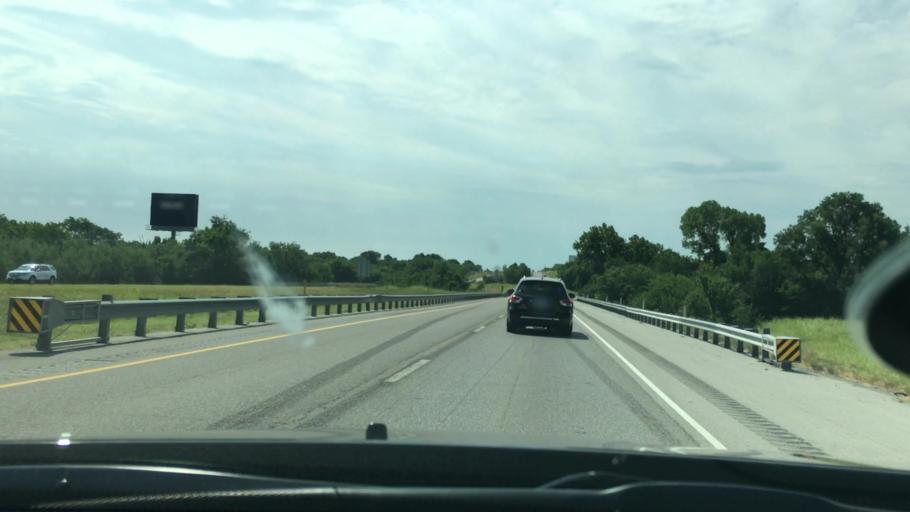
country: US
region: Oklahoma
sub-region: Murray County
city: Davis
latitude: 34.5021
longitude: -97.1716
